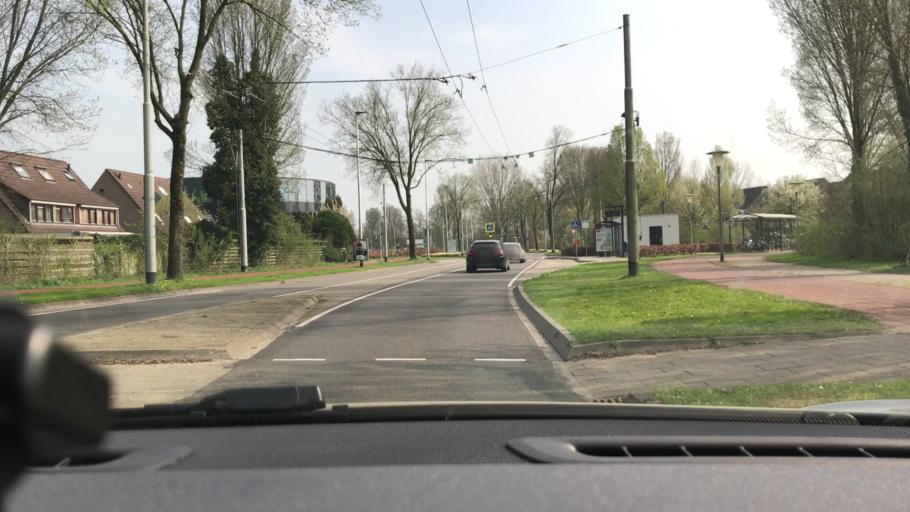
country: NL
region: Gelderland
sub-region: Gemeente Renkum
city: Oosterbeek
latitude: 51.9624
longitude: 5.8699
